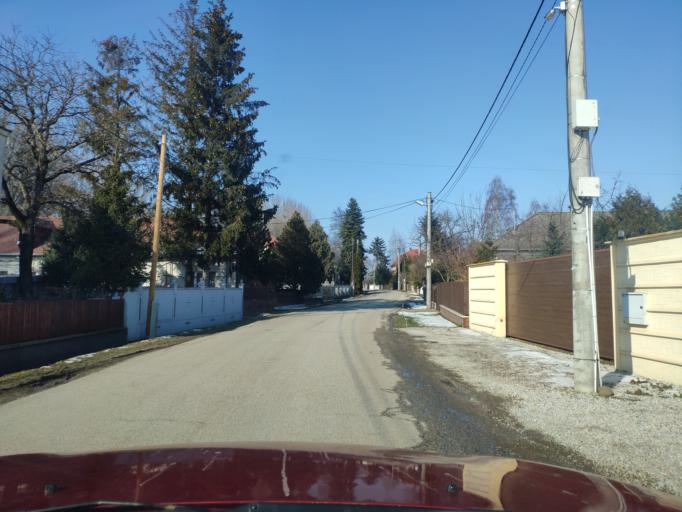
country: HU
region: Borsod-Abauj-Zemplen
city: Gonc
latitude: 48.5825
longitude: 21.2721
